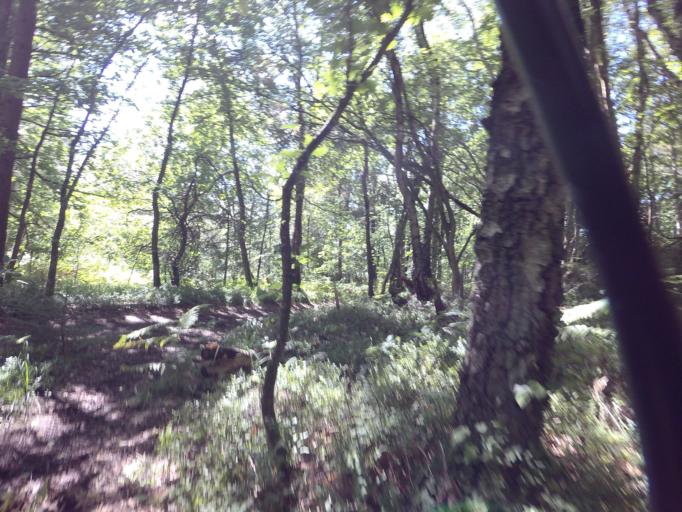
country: DK
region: Central Jutland
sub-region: Silkeborg Kommune
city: Svejbaek
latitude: 56.2163
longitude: 9.6978
